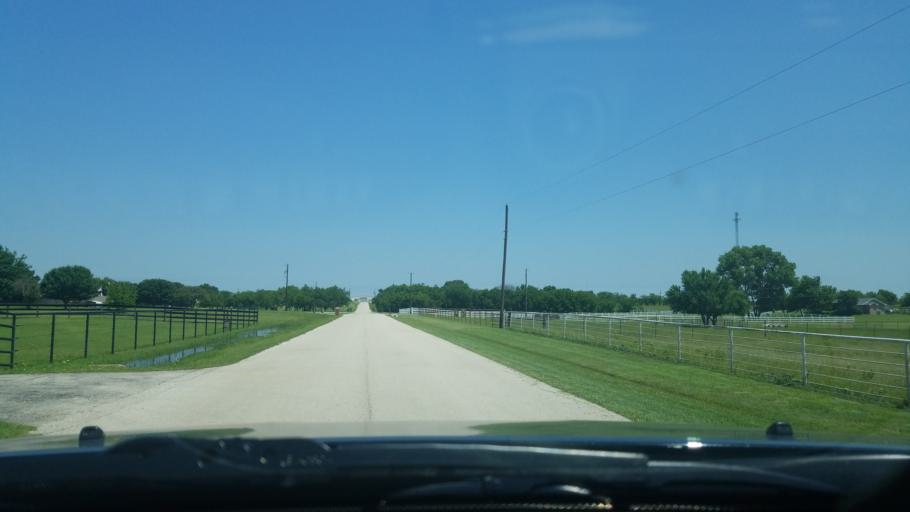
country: US
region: Texas
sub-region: Denton County
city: Krum
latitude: 33.2385
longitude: -97.2590
